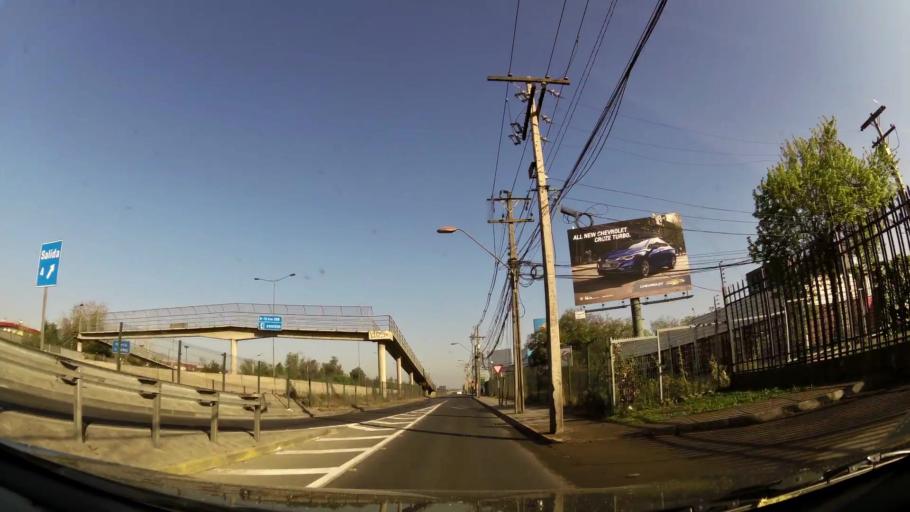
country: CL
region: Santiago Metropolitan
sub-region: Provincia de Santiago
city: Santiago
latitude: -33.3781
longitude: -70.6516
